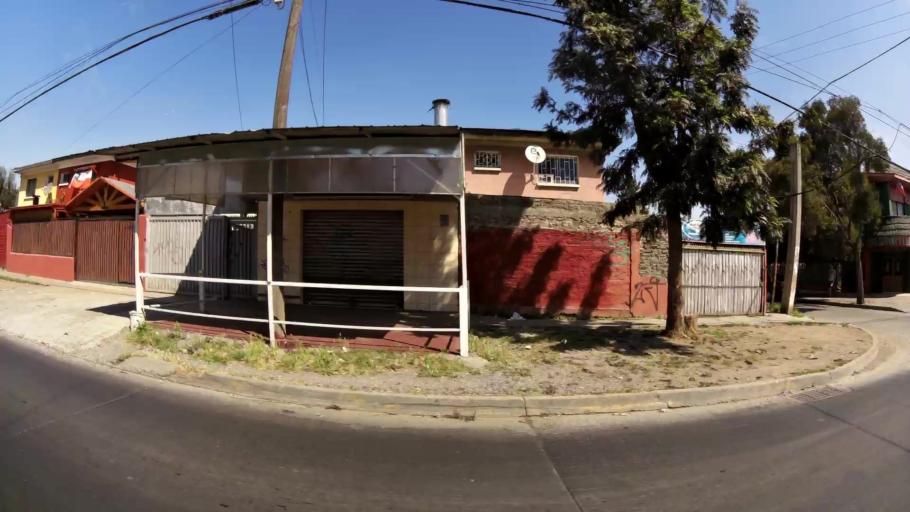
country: CL
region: Santiago Metropolitan
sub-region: Provincia de Santiago
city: Lo Prado
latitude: -33.4077
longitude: -70.6976
